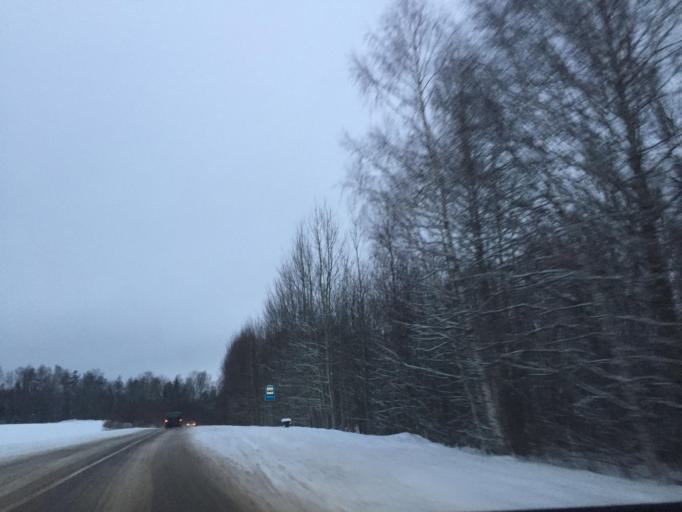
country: LV
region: Raunas
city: Rauna
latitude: 57.4309
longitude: 25.6946
